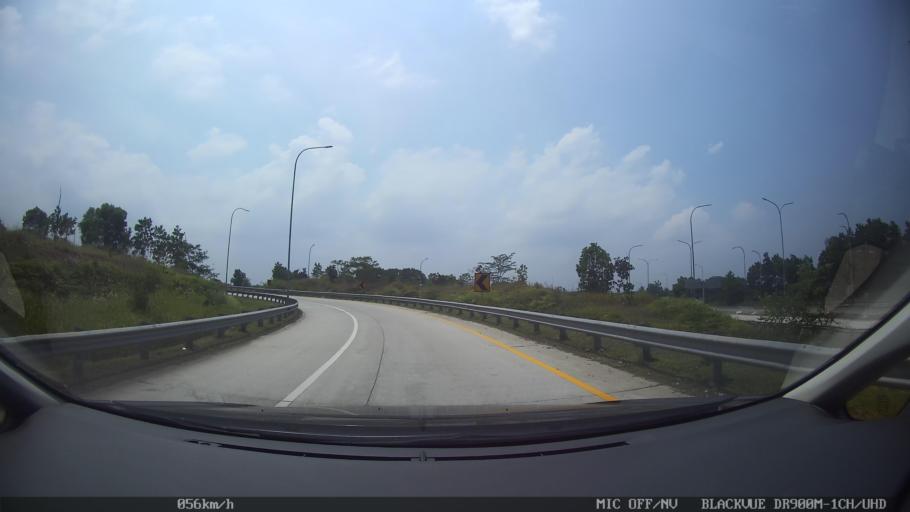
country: ID
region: Lampung
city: Panjang
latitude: -5.3964
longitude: 105.3499
